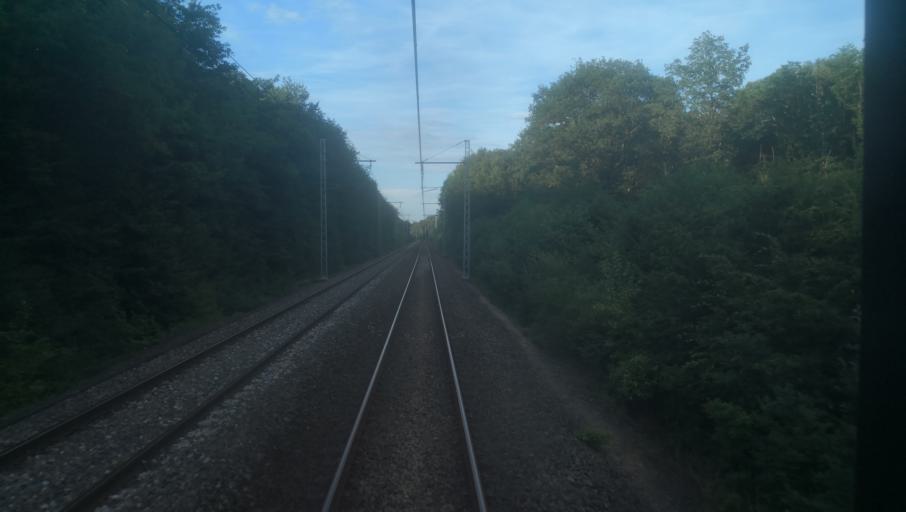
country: FR
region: Centre
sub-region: Departement de l'Indre
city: Saint-Marcel
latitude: 46.6633
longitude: 1.5335
